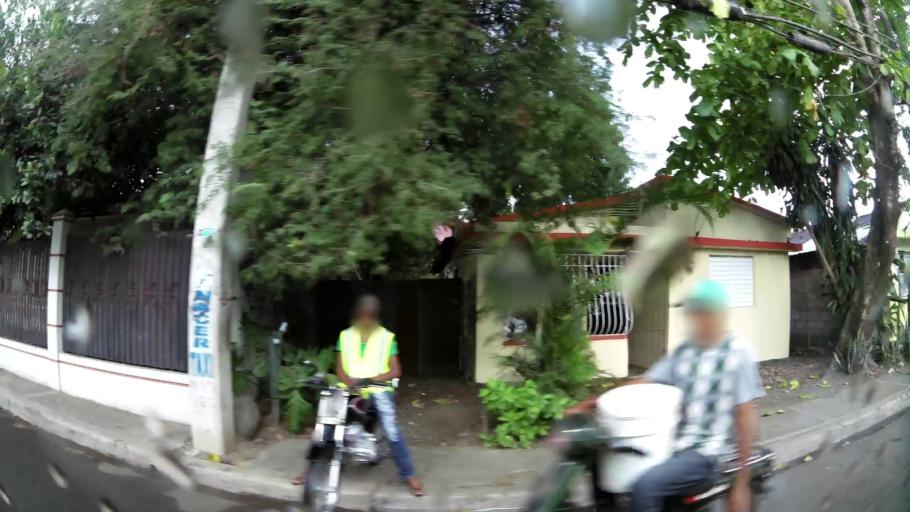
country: DO
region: Monsenor Nouel
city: Bonao
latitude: 18.9307
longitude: -70.4010
